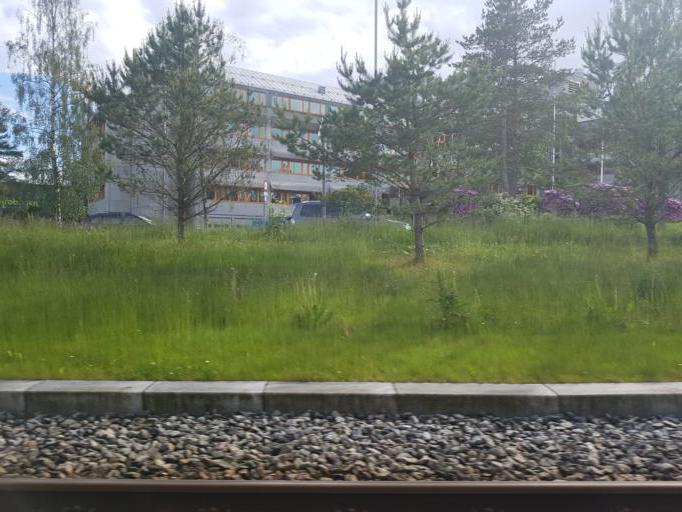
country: NO
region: Hordaland
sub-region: Bergen
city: Ytrebygda
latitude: 60.2976
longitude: 5.2784
